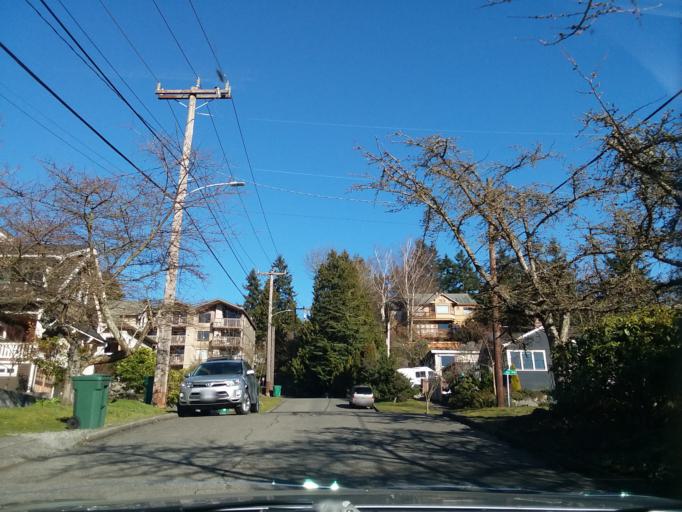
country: US
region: Washington
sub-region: King County
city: Seattle
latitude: 47.6615
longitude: -122.3587
